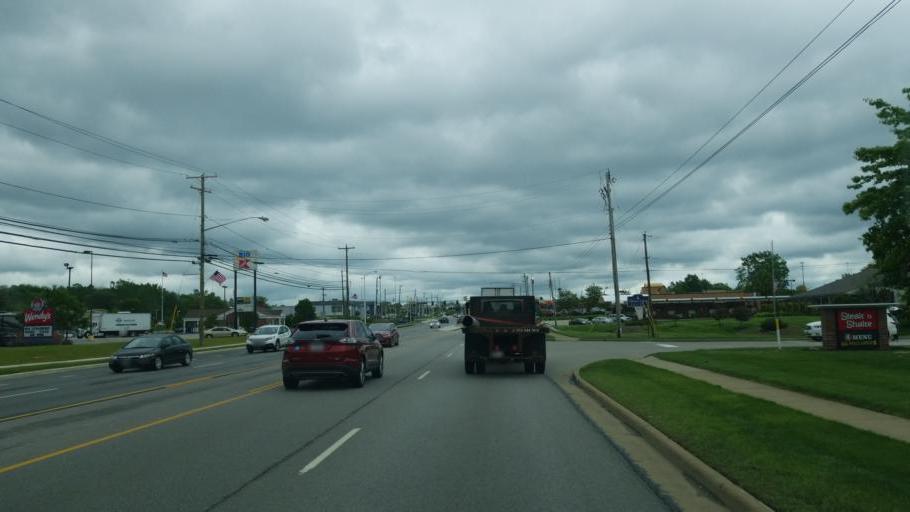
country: US
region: Ohio
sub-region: Medina County
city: Brunswick
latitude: 41.2382
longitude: -81.8061
